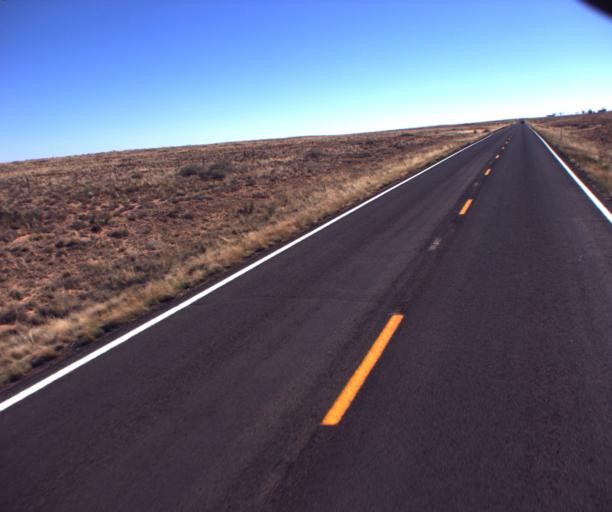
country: US
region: Arizona
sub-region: Coconino County
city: Tuba City
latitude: 35.9658
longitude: -110.9512
